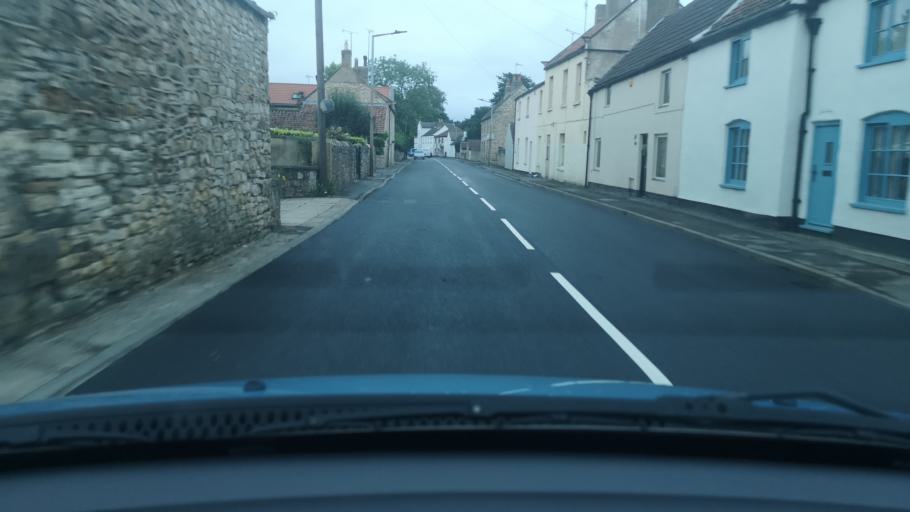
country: GB
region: England
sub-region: Doncaster
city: Campsall
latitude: 53.6186
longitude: -1.1826
